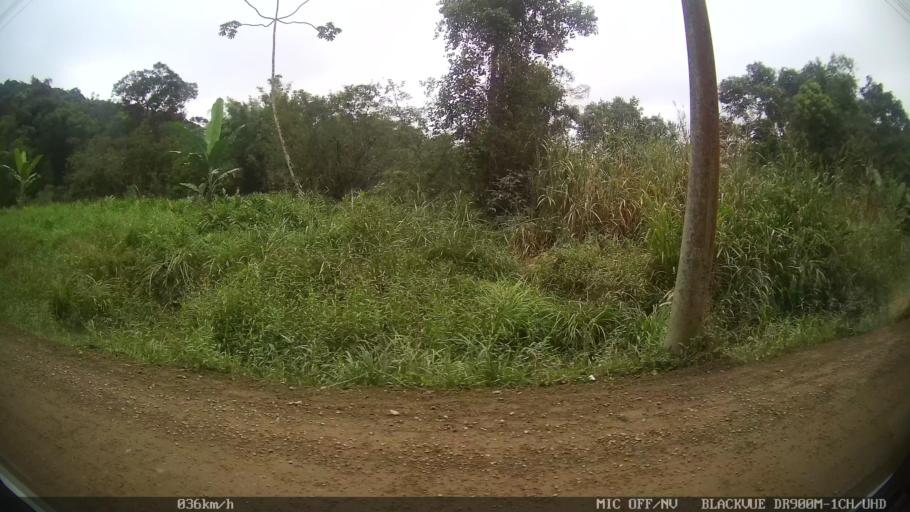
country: BR
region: Santa Catarina
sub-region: Joinville
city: Joinville
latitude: -26.2486
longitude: -48.9249
